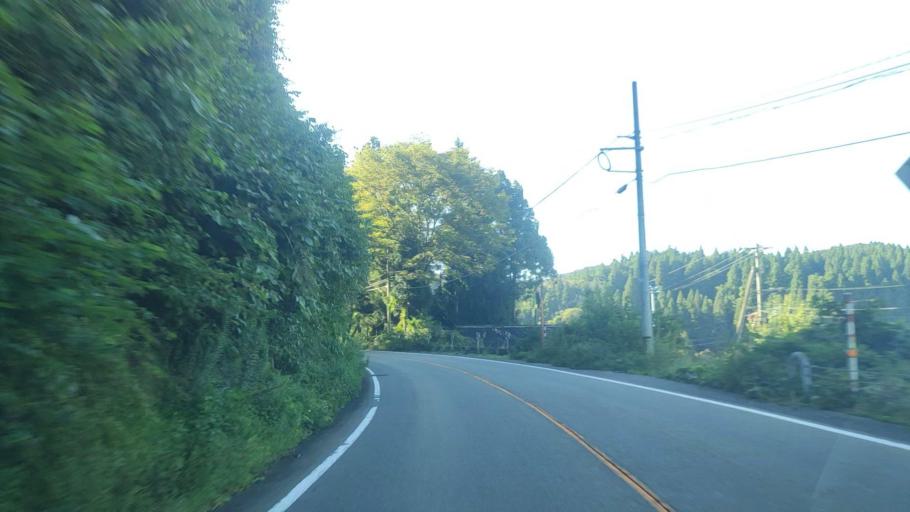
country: JP
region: Ishikawa
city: Nanao
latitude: 37.2831
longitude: 137.0348
